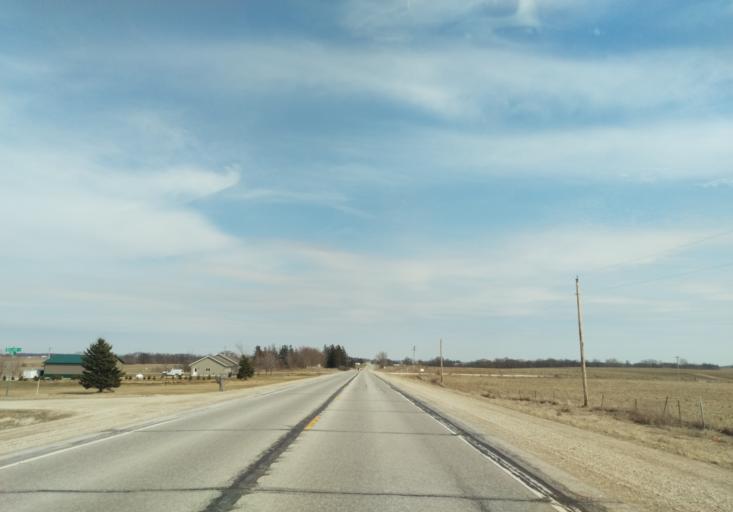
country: US
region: Iowa
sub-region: Allamakee County
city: Waukon
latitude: 43.2407
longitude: -91.5899
